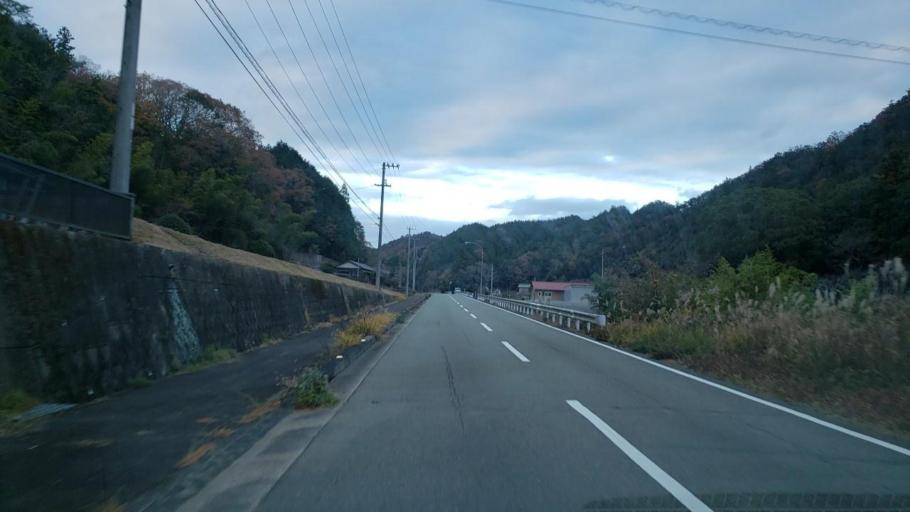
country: JP
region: Tokushima
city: Kamojimacho-jogejima
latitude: 34.1854
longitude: 134.2515
